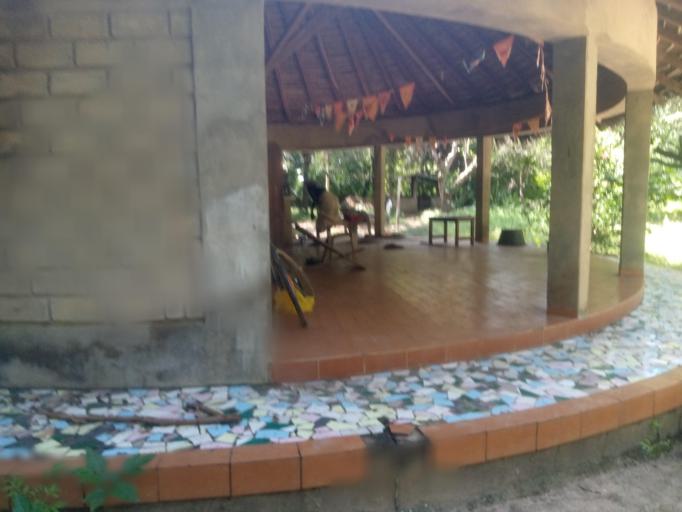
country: GM
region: Western
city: Gunjur
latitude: 13.0382
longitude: -16.7293
